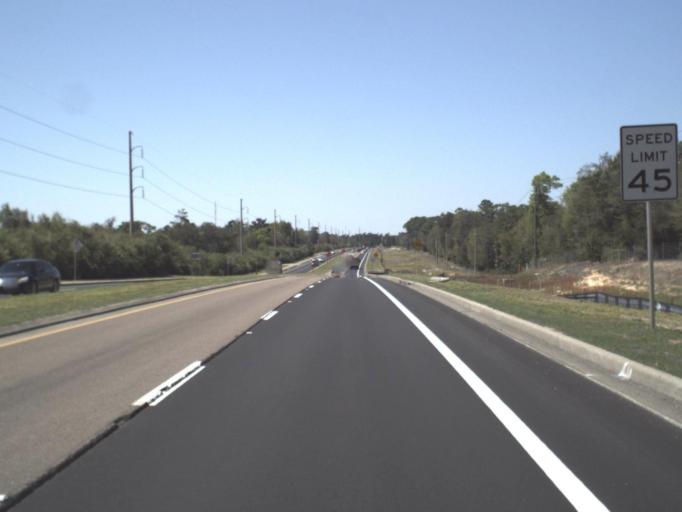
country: US
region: Florida
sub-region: Okaloosa County
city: Niceville
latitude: 30.4902
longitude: -86.4255
